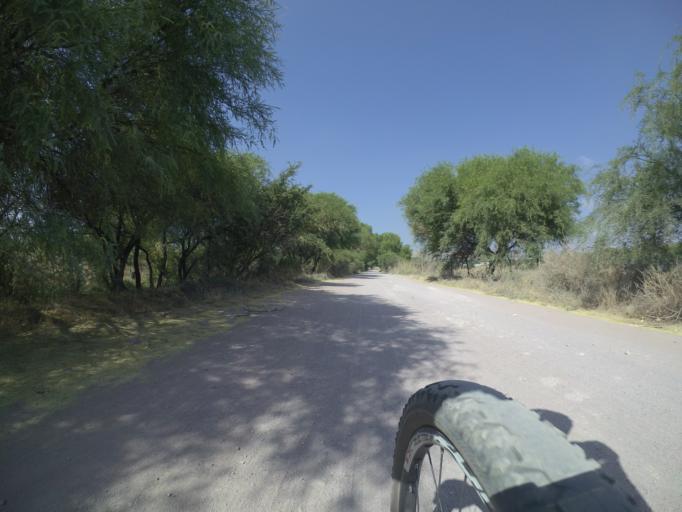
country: MX
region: Aguascalientes
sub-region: Jesus Maria
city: Paseos de las Haciendas [Fraccionamiento]
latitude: 22.0002
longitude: -102.3505
